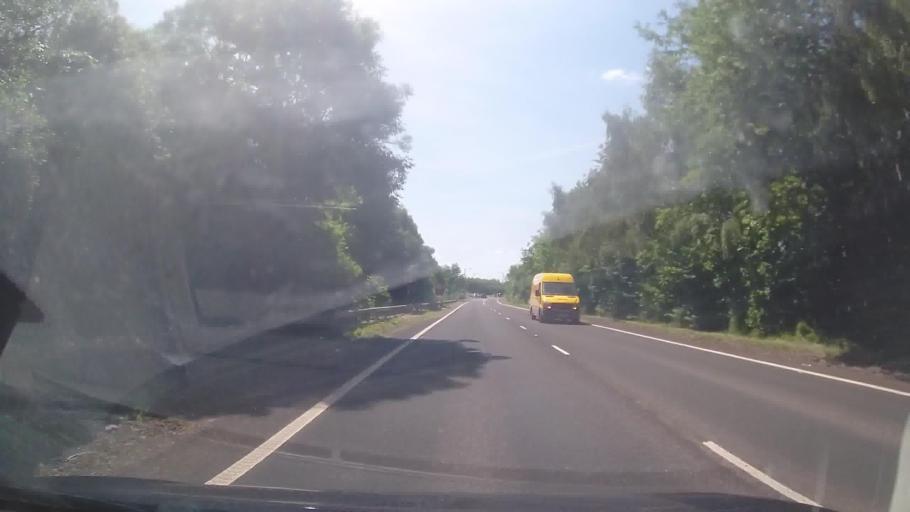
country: GB
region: England
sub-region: Herefordshire
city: Leominster
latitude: 52.2237
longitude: -2.7272
